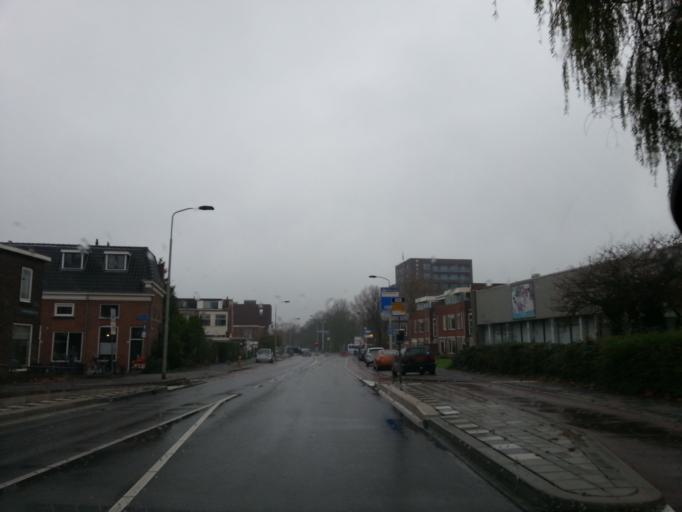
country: NL
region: South Holland
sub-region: Gemeente Delft
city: Delft
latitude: 52.0132
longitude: 4.3680
